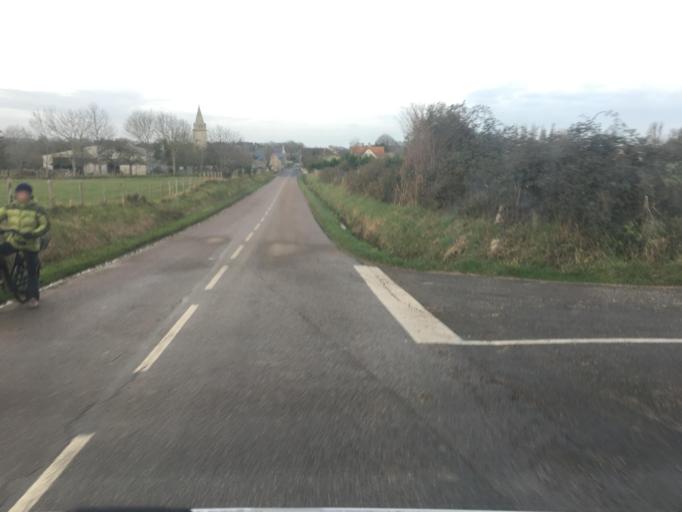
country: FR
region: Lower Normandy
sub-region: Departement du Calvados
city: Ver-sur-Mer
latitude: 49.3256
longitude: -0.5609
